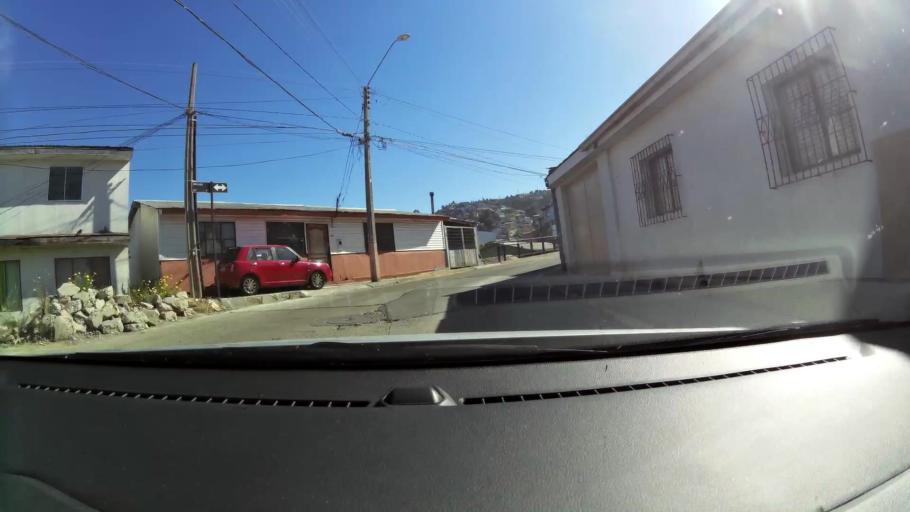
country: CL
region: Valparaiso
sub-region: Provincia de Valparaiso
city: Valparaiso
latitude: -33.0556
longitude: -71.6173
